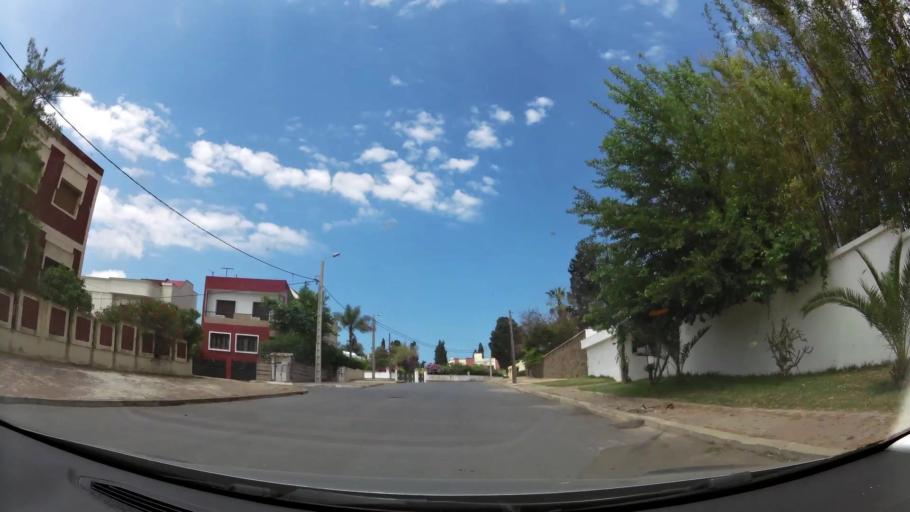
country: MA
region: Gharb-Chrarda-Beni Hssen
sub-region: Kenitra Province
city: Kenitra
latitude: 34.2663
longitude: -6.5942
